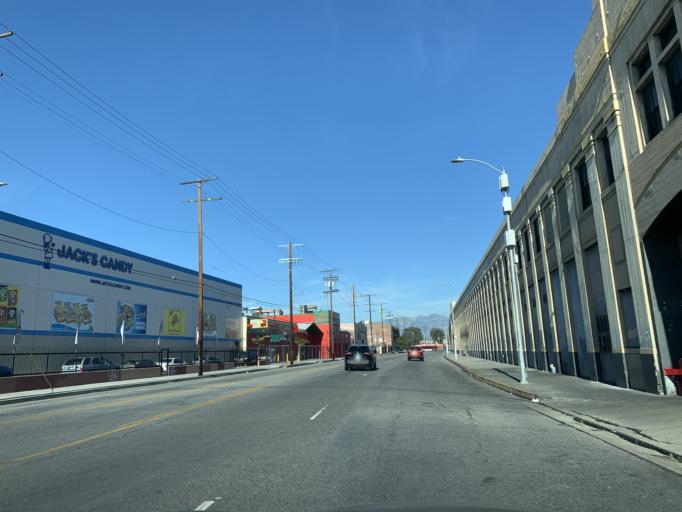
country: US
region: California
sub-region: Los Angeles County
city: Los Angeles
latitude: 34.0346
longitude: -118.2426
